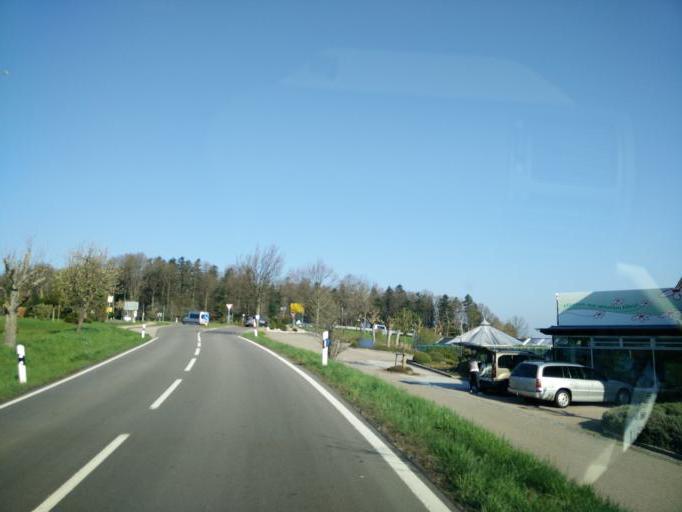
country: DE
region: Baden-Wuerttemberg
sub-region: Karlsruhe Region
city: Engelsbrand
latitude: 48.8308
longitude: 8.6659
